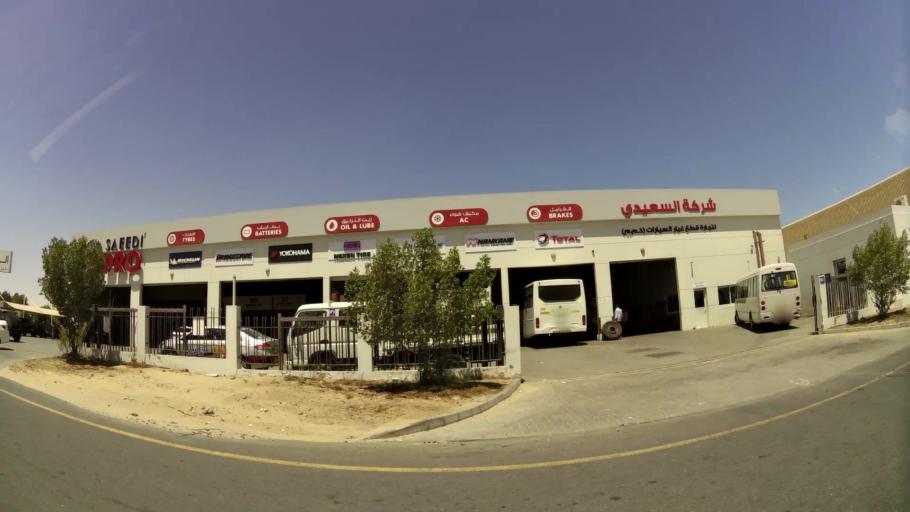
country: AE
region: Dubai
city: Dubai
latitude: 24.9734
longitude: 55.1897
